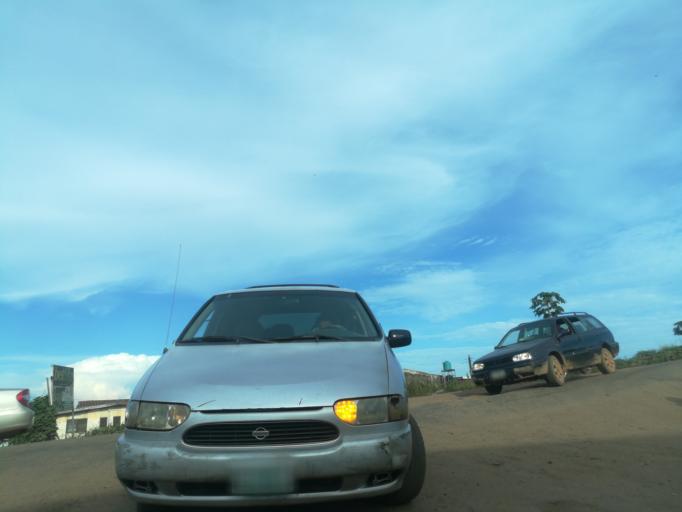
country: NG
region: Oyo
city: Ibadan
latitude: 7.3461
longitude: 3.9161
